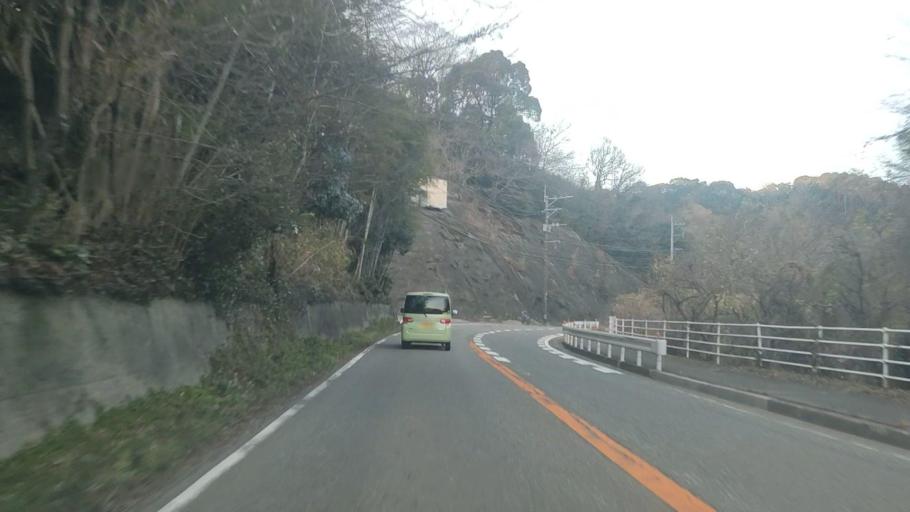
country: JP
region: Fukuoka
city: Dazaifu
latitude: 33.5427
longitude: 130.5393
